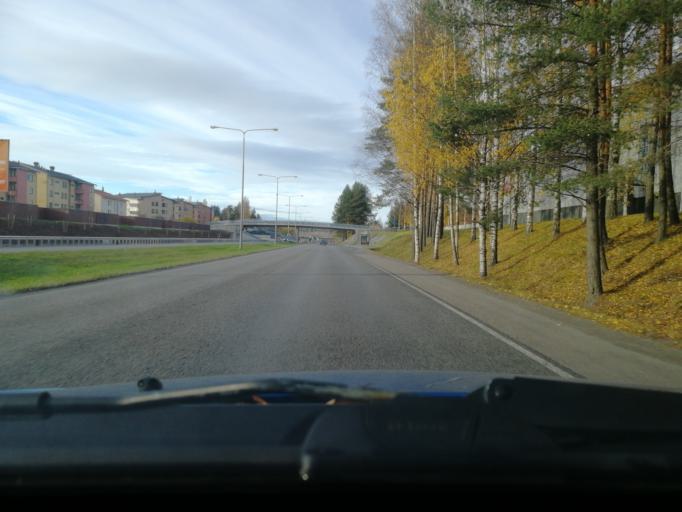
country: FI
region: Pirkanmaa
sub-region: Tampere
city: Tampere
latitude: 61.4755
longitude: 23.8362
